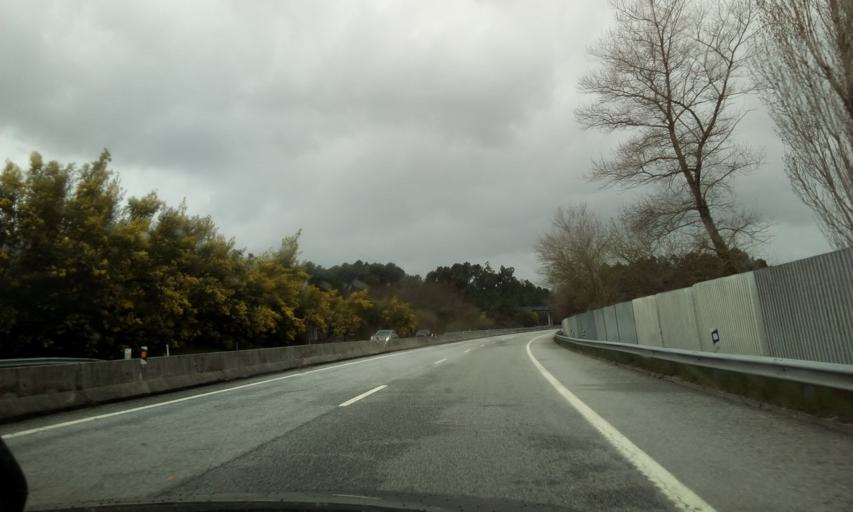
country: PT
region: Viseu
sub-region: Viseu
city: Rio de Loba
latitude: 40.6445
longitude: -7.8708
